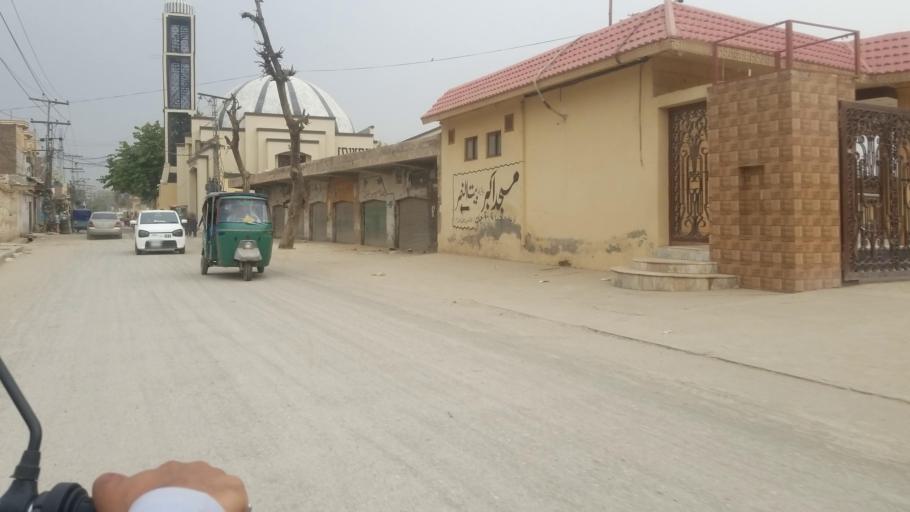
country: PK
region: Khyber Pakhtunkhwa
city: Peshawar
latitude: 33.9855
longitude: 71.5542
